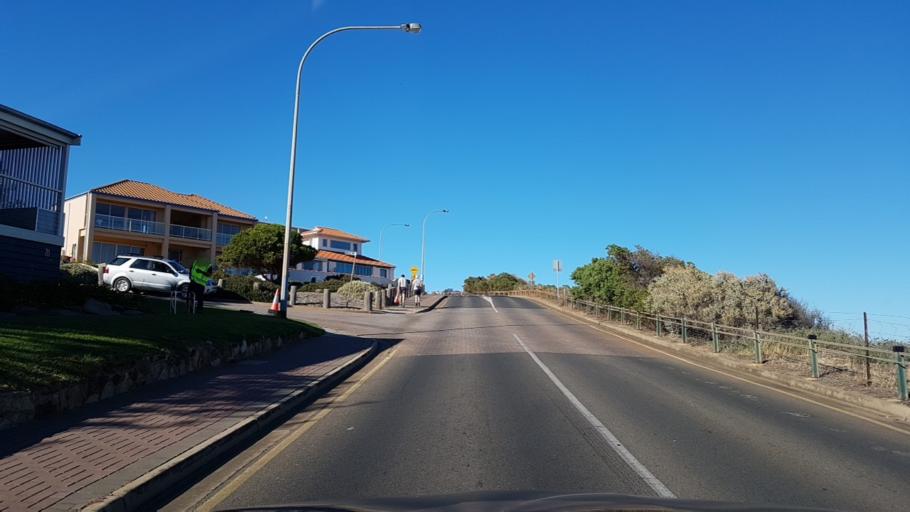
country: AU
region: South Australia
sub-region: Adelaide
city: Port Noarlunga
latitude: -35.1425
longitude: 138.4685
